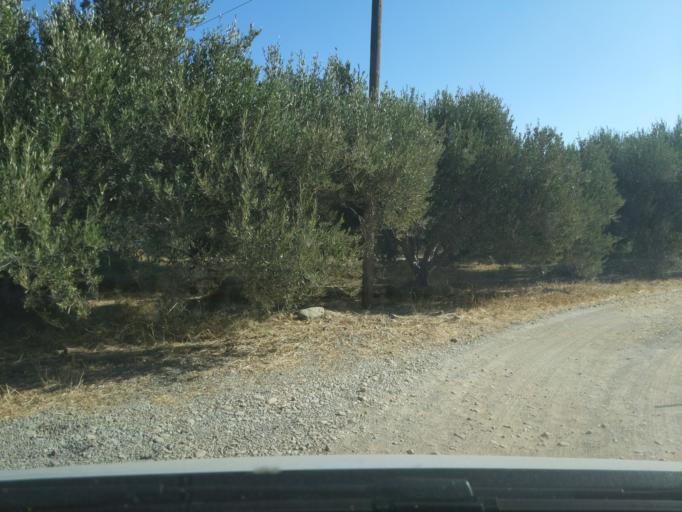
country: GR
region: Crete
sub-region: Nomos Lasithiou
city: Palekastro
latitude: 35.2123
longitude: 26.2659
